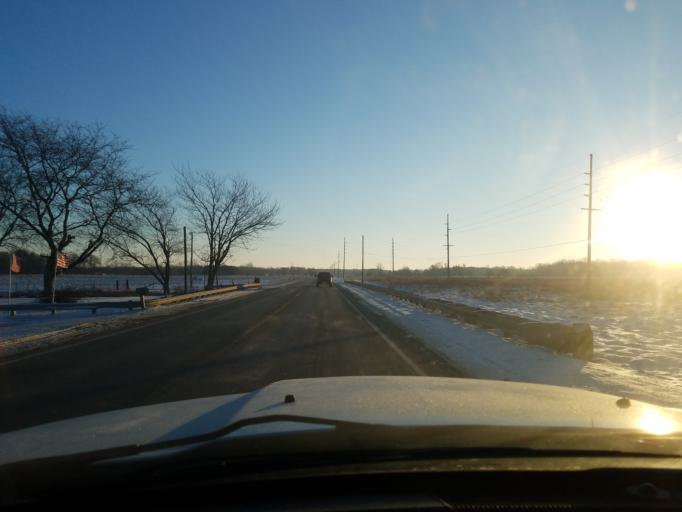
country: US
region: Indiana
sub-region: Marshall County
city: Bremen
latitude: 41.4537
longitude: -86.1145
